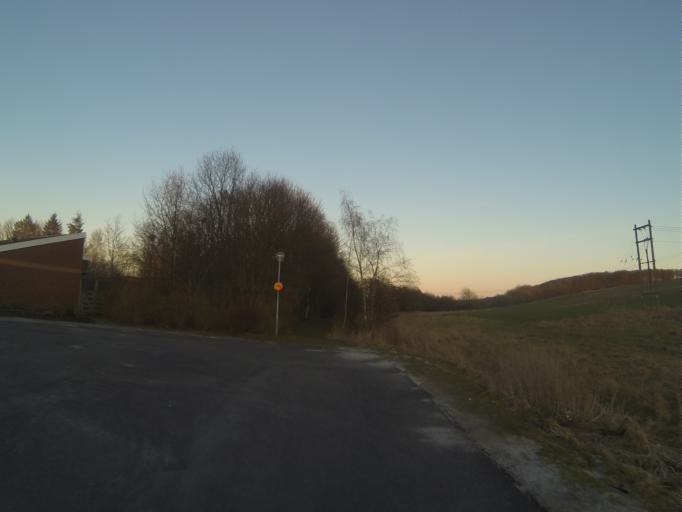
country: SE
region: Skane
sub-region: Lunds Kommun
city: Genarp
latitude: 55.7136
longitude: 13.3465
